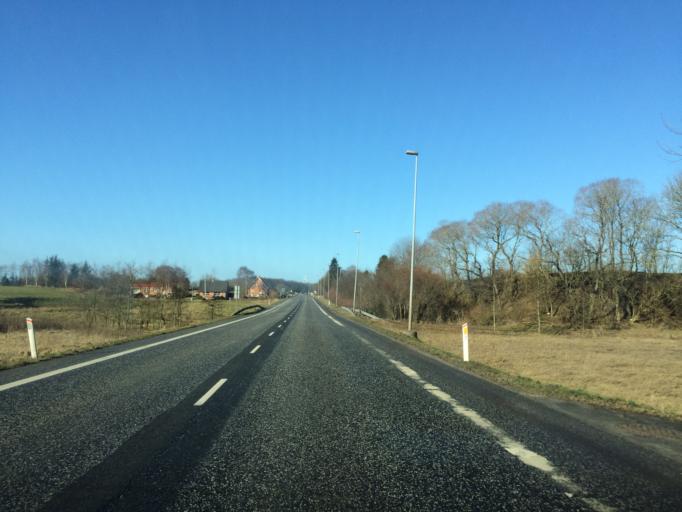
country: DK
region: Central Jutland
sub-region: Viborg Kommune
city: Stoholm
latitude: 56.4355
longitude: 9.1293
